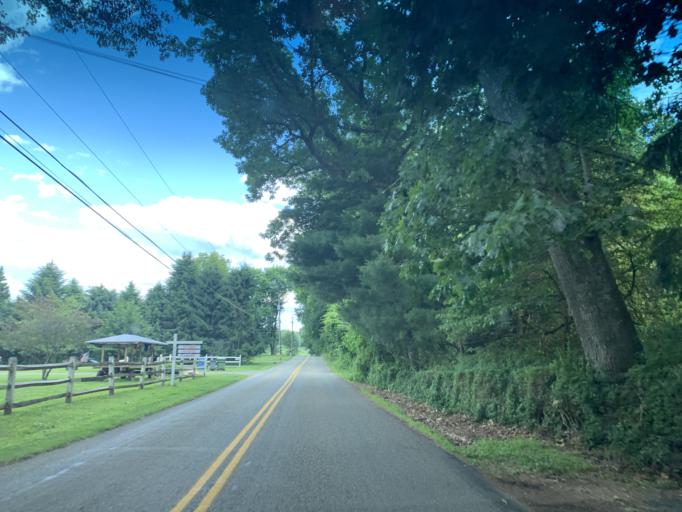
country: US
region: Maryland
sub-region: Harford County
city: Fallston
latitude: 39.5571
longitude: -76.4472
